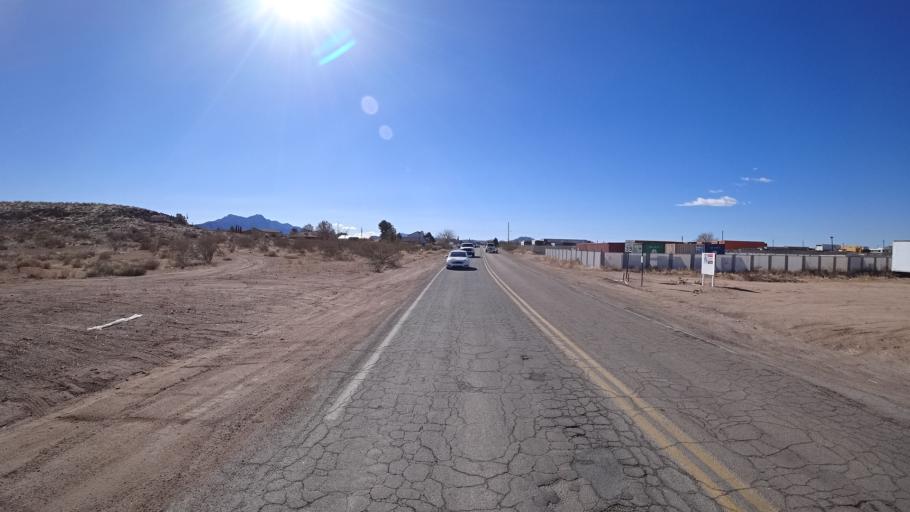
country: US
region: Arizona
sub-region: Mohave County
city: Kingman
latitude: 35.2102
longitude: -114.0114
